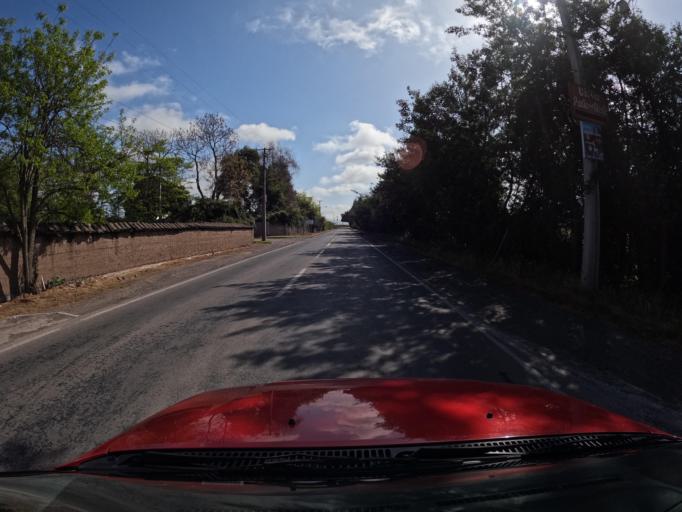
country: CL
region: Maule
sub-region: Provincia de Curico
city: Rauco
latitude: -34.9039
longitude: -71.2774
